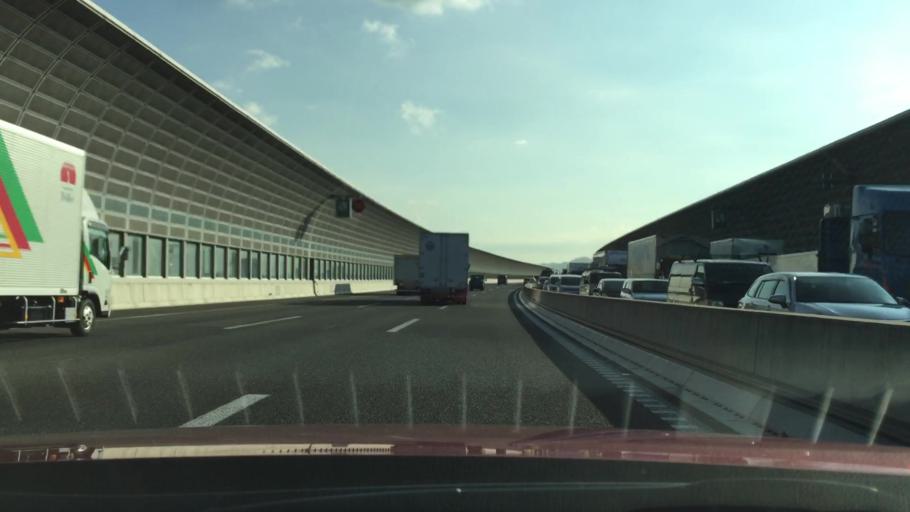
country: JP
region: Osaka
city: Neyagawa
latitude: 34.7436
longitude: 135.6200
